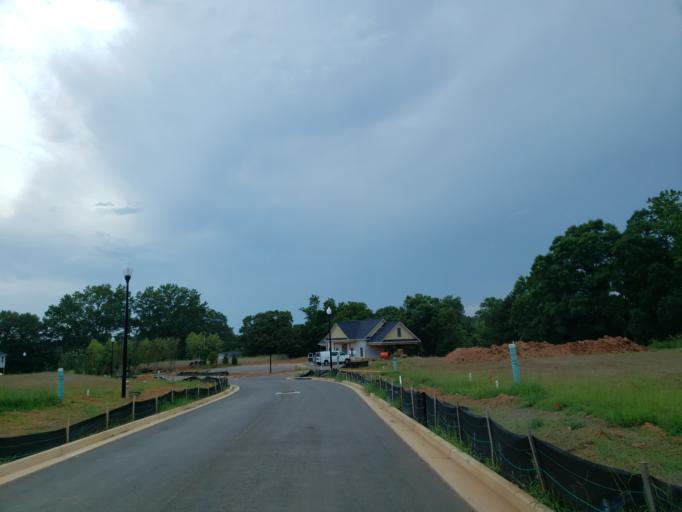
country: US
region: Georgia
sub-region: Cherokee County
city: Holly Springs
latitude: 34.1796
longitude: -84.4260
